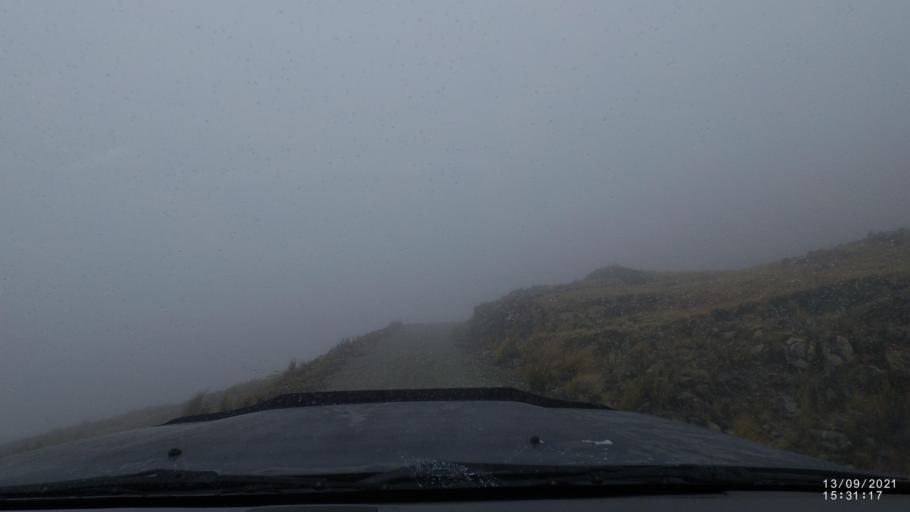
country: BO
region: Cochabamba
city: Colomi
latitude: -17.3420
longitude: -65.7519
